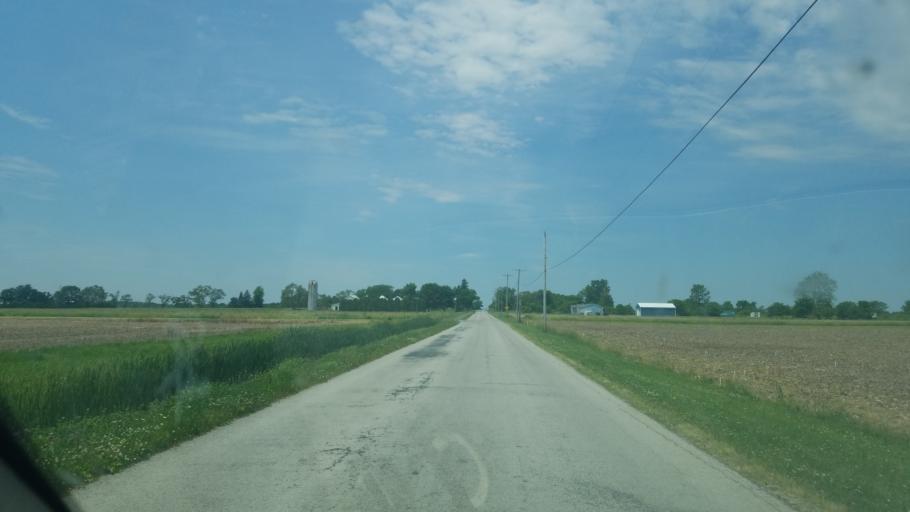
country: US
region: Ohio
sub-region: Wood County
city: North Baltimore
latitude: 41.2539
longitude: -83.6198
